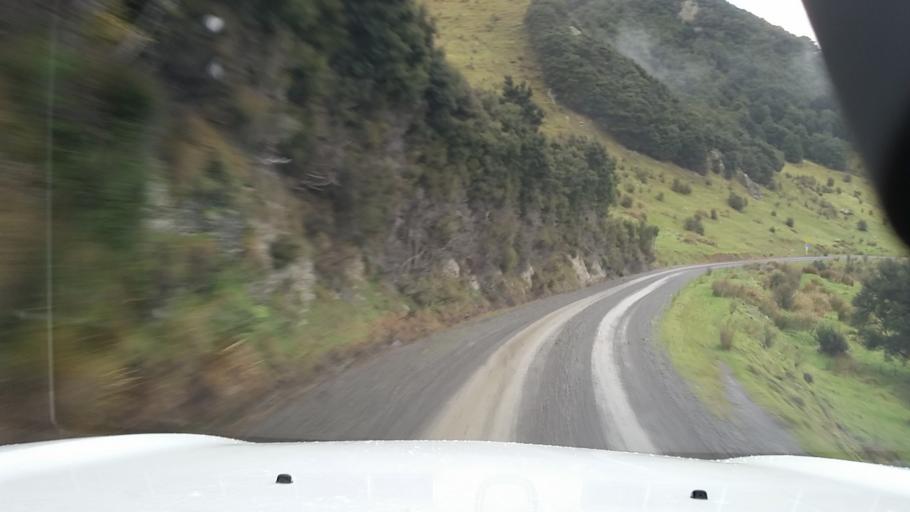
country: NZ
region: Wellington
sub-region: South Wairarapa District
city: Waipawa
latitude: -41.3605
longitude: 175.7019
